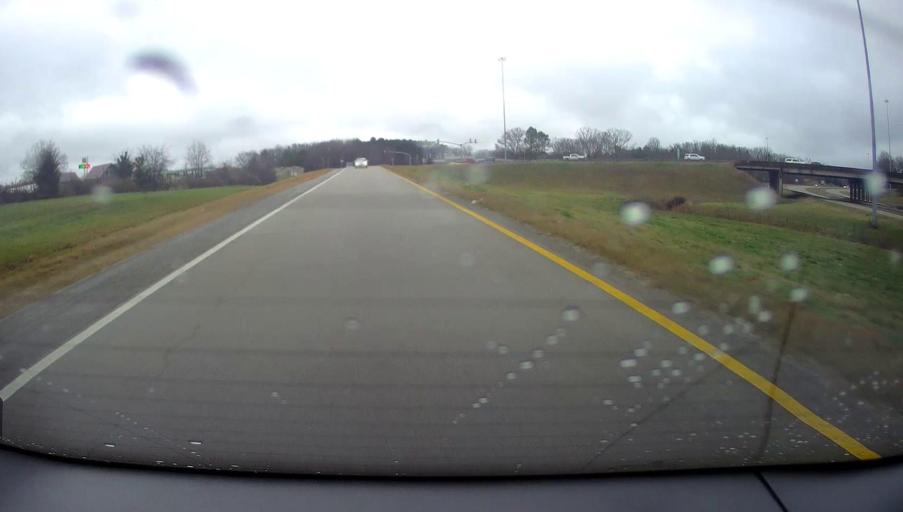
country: US
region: Mississippi
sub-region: Alcorn County
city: Corinth
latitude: 34.9295
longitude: -88.5482
